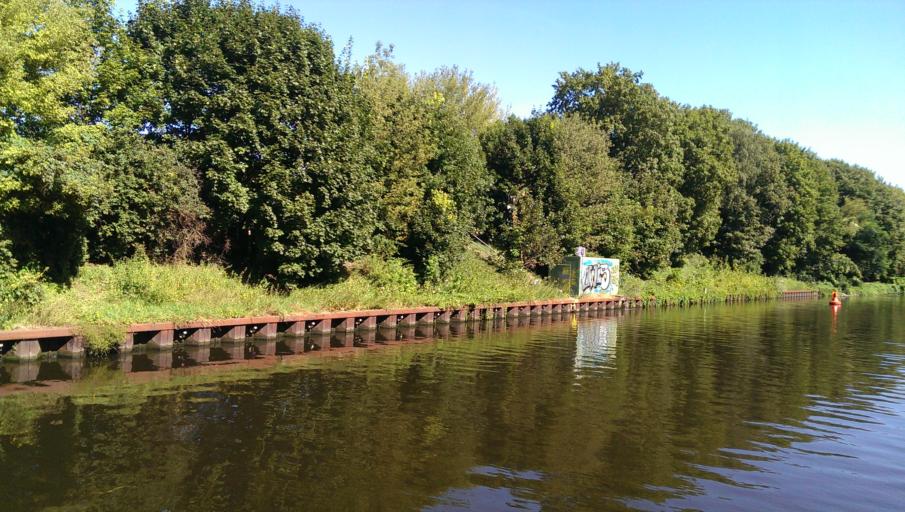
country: DE
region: Brandenburg
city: Teltow
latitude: 52.4054
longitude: 13.2508
